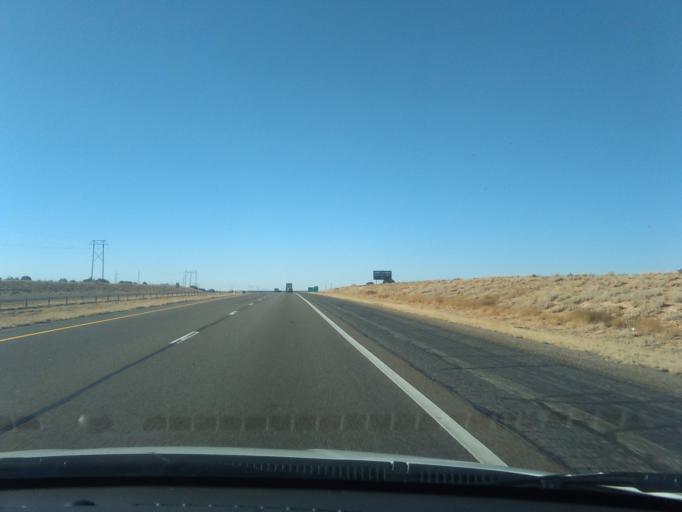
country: US
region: New Mexico
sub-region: Sandoval County
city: Santo Domingo Pueblo
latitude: 35.4745
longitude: -106.2946
